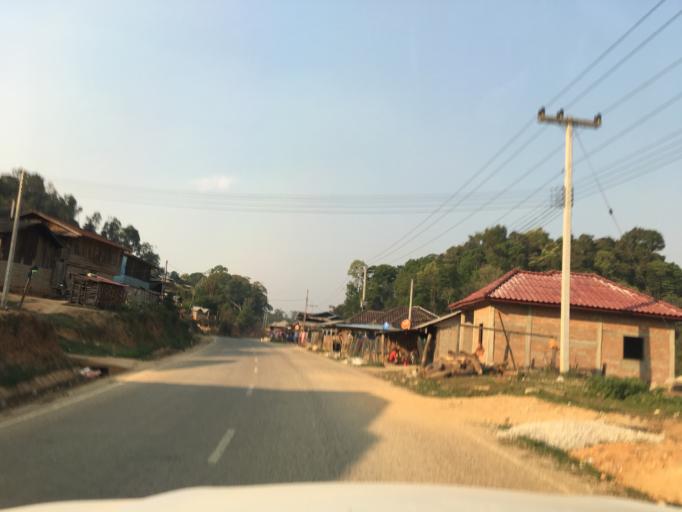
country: LA
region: Houaphan
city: Xam Nua
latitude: 20.5951
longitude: 104.0679
